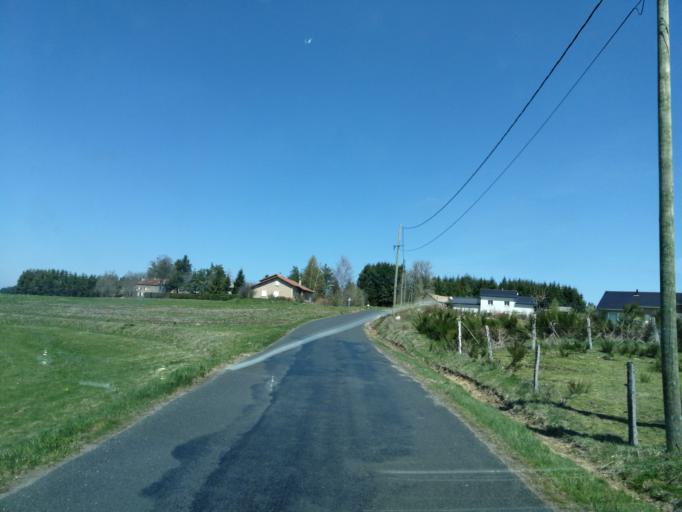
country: FR
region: Rhone-Alpes
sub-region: Departement de l'Ardeche
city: Saint-Agreve
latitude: 44.9731
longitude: 4.4224
